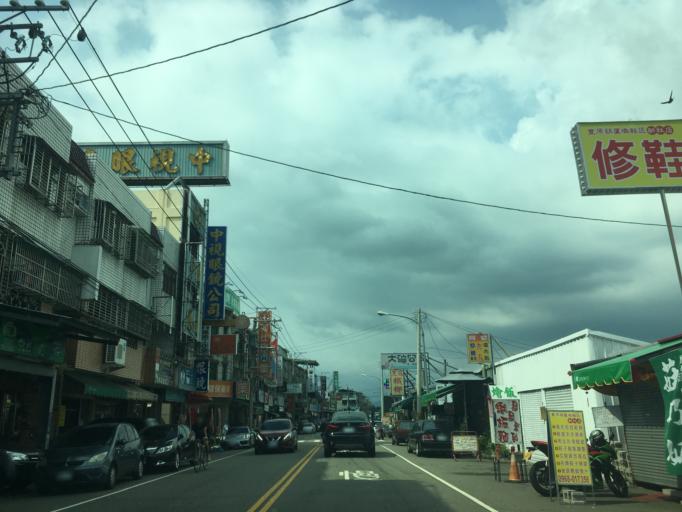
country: TW
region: Taiwan
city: Fengyuan
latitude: 24.2399
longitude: 120.8076
